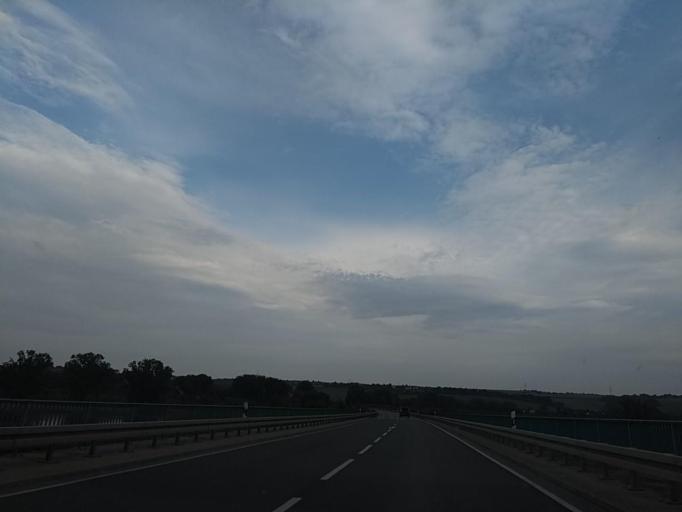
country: DE
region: Saxony-Anhalt
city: Kretzschau
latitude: 51.0444
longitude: 12.1015
